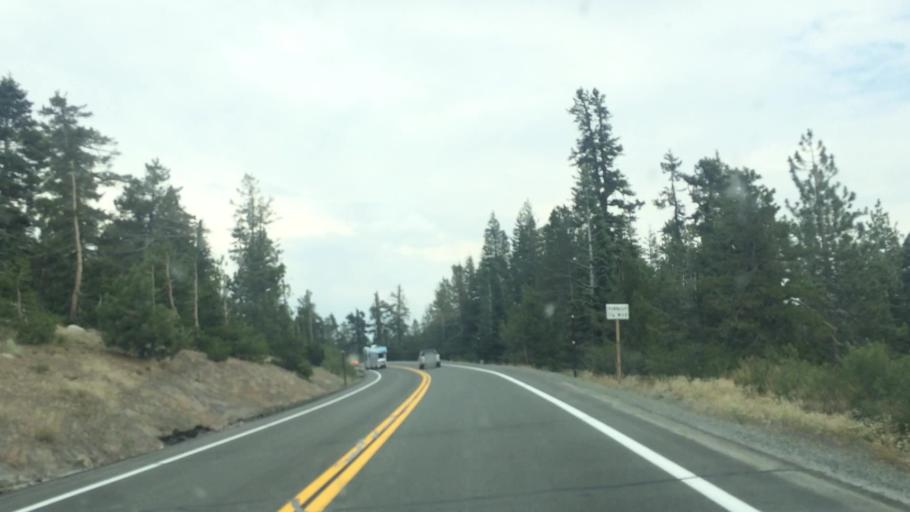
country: US
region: California
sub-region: El Dorado County
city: South Lake Tahoe
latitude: 38.6326
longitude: -120.1605
